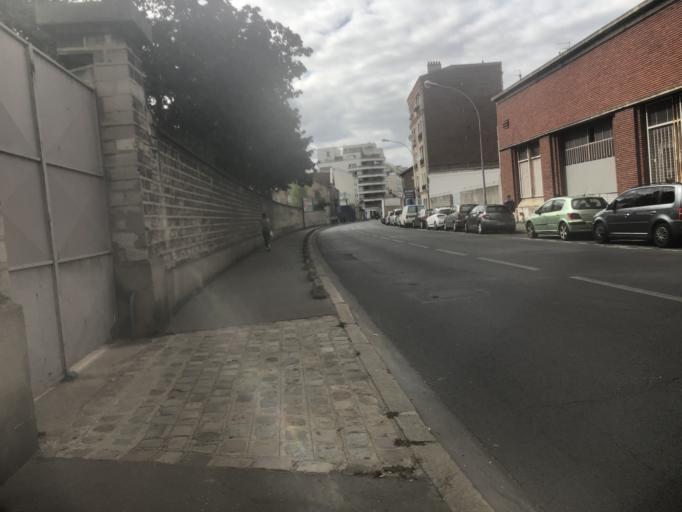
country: FR
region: Ile-de-France
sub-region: Paris
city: Saint-Ouen
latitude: 48.9146
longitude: 2.3400
